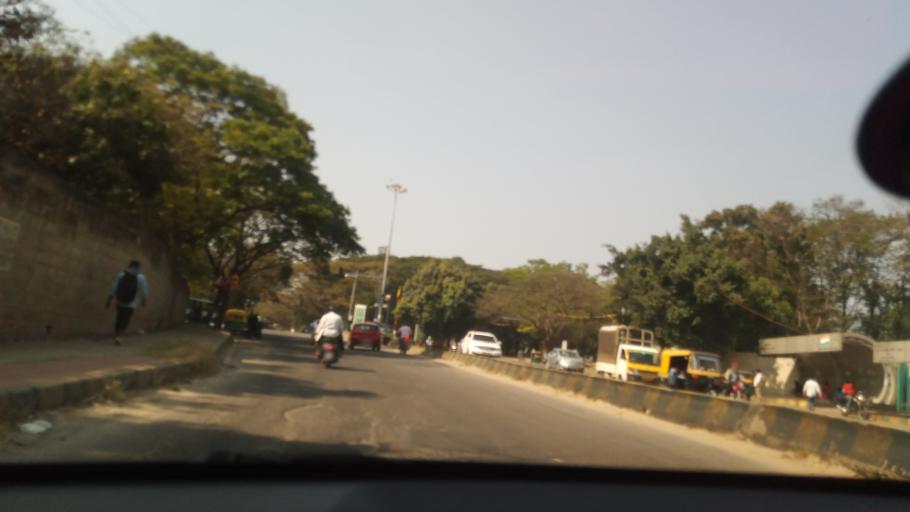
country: IN
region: Karnataka
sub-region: Bangalore Urban
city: Yelahanka
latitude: 13.0448
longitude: 77.5568
